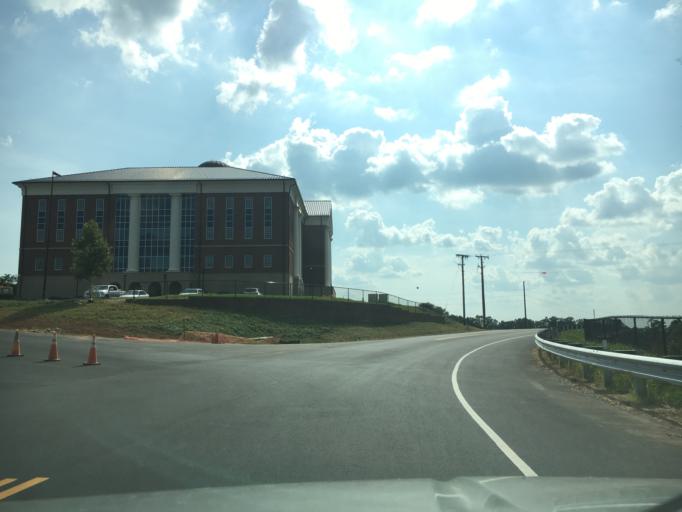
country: US
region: Virginia
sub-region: City of Lynchburg
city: West Lynchburg
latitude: 37.3382
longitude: -79.1786
